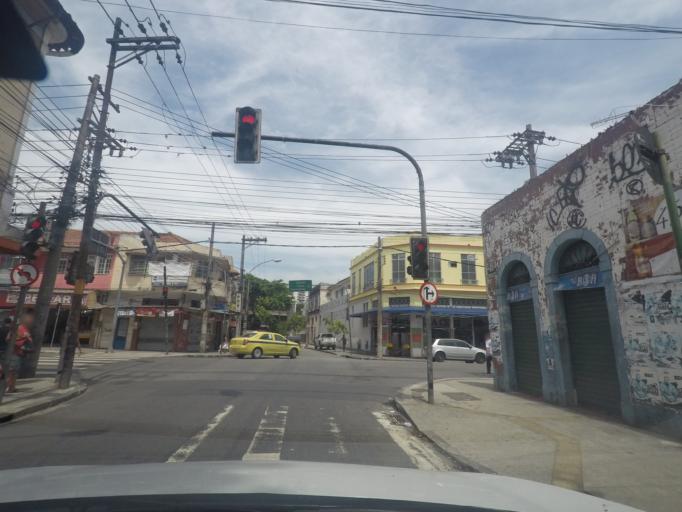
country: BR
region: Rio de Janeiro
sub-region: Rio De Janeiro
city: Rio de Janeiro
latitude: -22.9234
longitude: -43.2085
